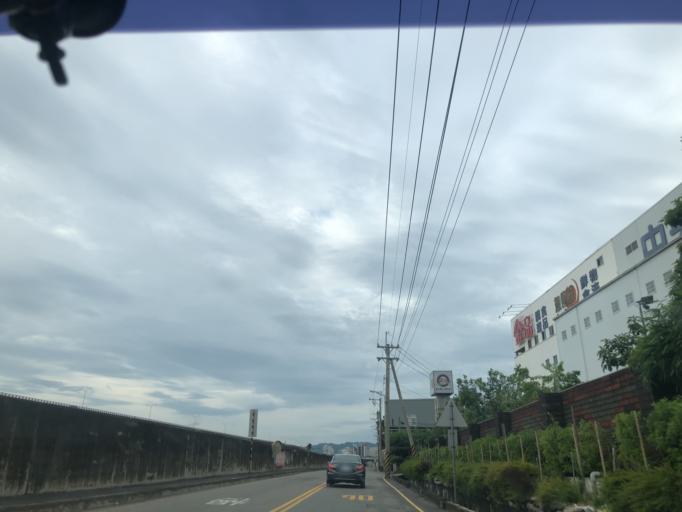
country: TW
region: Taiwan
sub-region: Taichung City
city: Taichung
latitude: 24.1249
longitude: 120.7048
